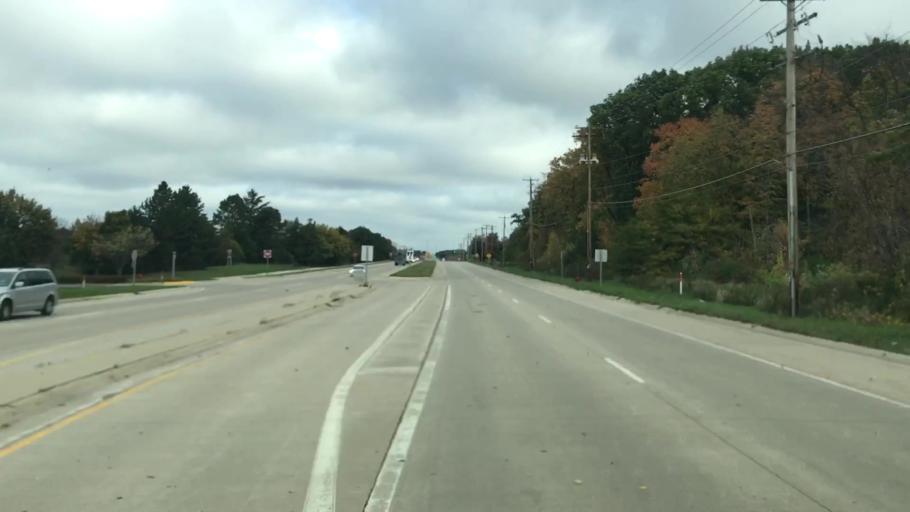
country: US
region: Wisconsin
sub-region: Waukesha County
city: Pewaukee
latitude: 43.0564
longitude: -88.2252
